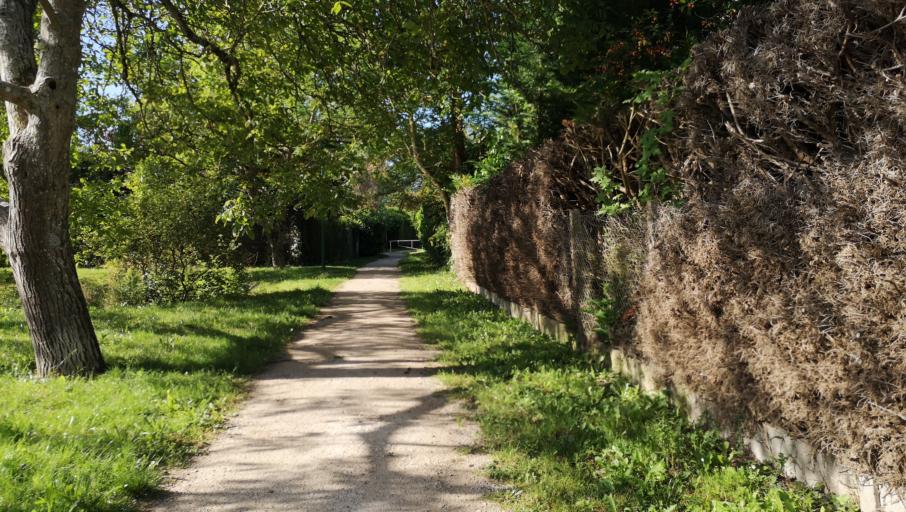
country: FR
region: Centre
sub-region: Departement du Loiret
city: Saint-Jean-de-Braye
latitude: 47.9167
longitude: 1.9727
